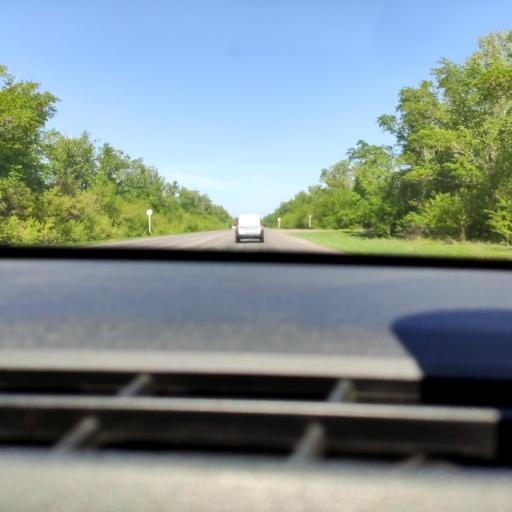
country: RU
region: Samara
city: Tol'yatti
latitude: 53.6003
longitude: 49.4090
